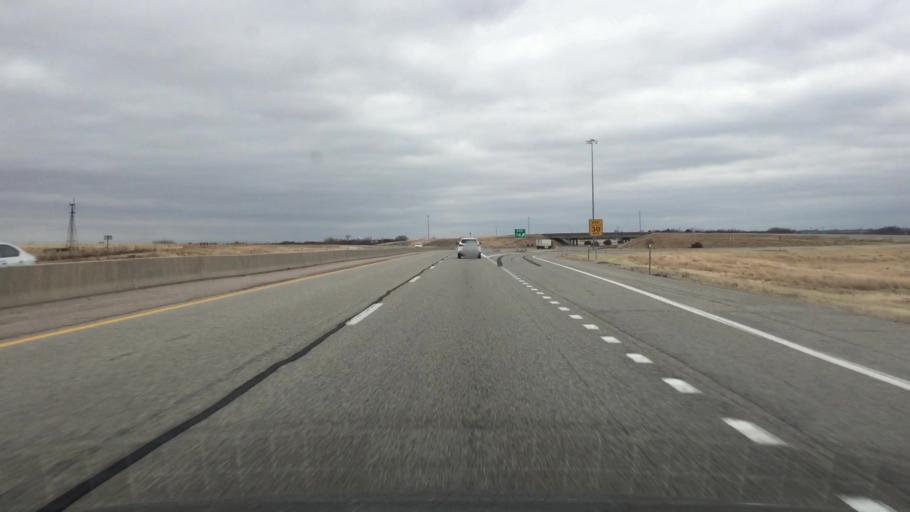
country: US
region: Kansas
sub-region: Butler County
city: El Dorado
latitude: 37.8797
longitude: -96.8434
